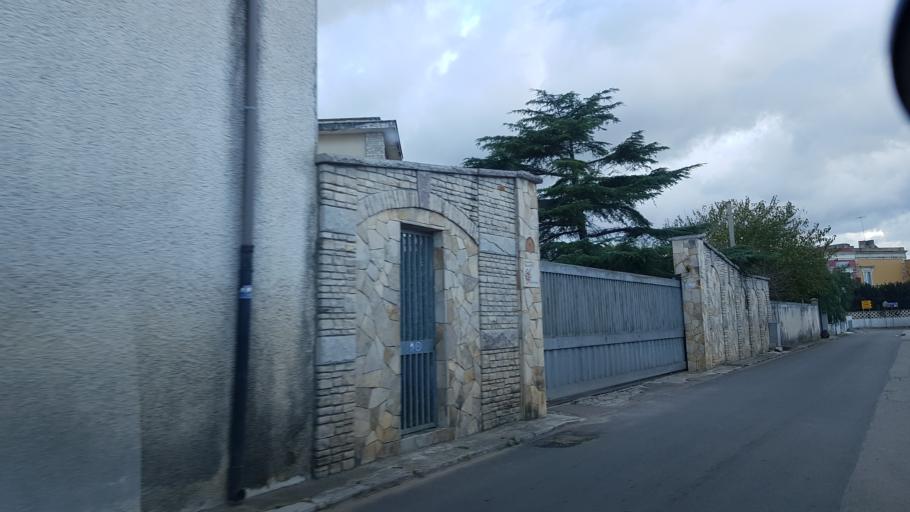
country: IT
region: Apulia
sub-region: Provincia di Brindisi
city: San Pietro Vernotico
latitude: 40.4917
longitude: 18.0008
